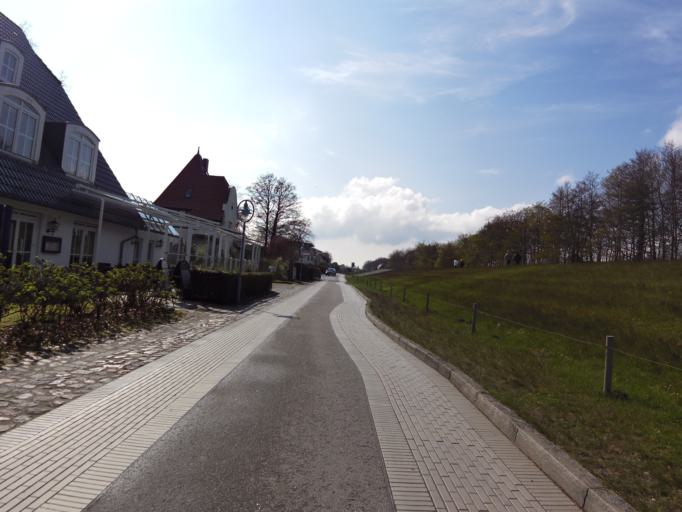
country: DE
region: Mecklenburg-Vorpommern
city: Zingst
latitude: 54.4409
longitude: 12.6885
